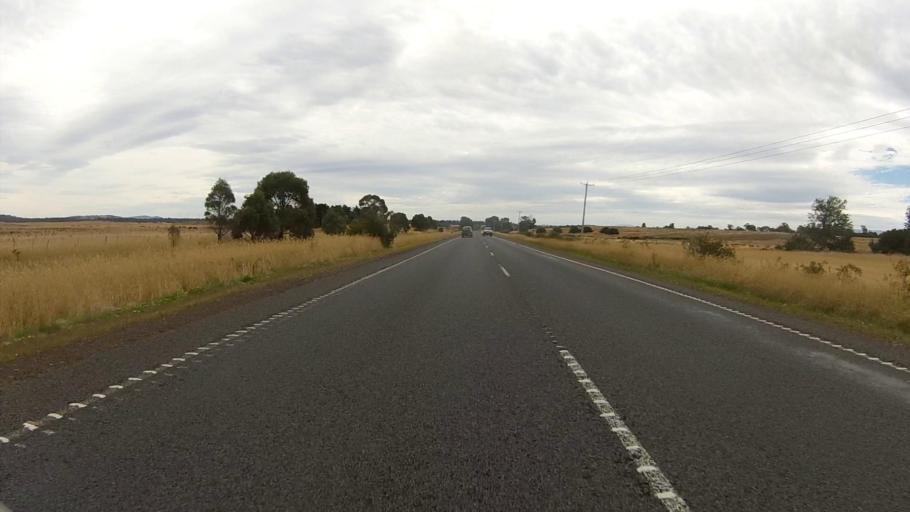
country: AU
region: Tasmania
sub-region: Northern Midlands
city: Evandale
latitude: -41.8555
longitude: 147.4533
